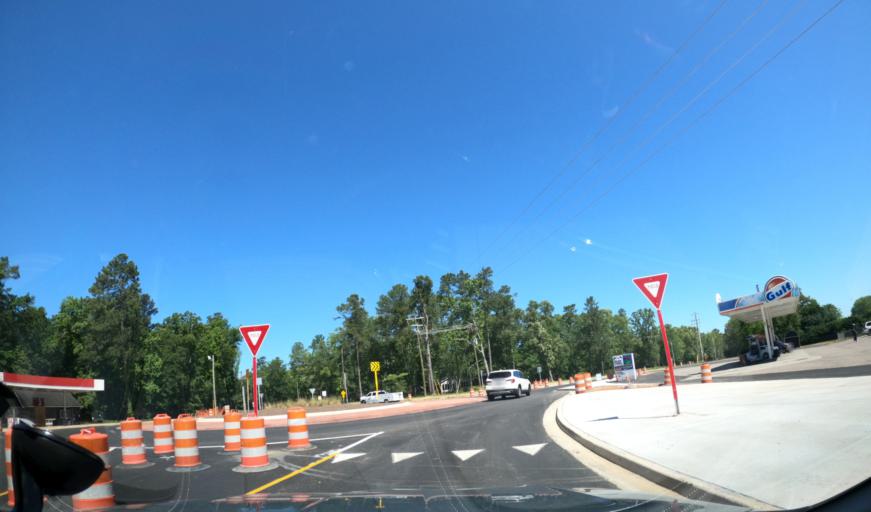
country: US
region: South Carolina
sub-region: Aiken County
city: Burnettown
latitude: 33.4588
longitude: -81.8485
